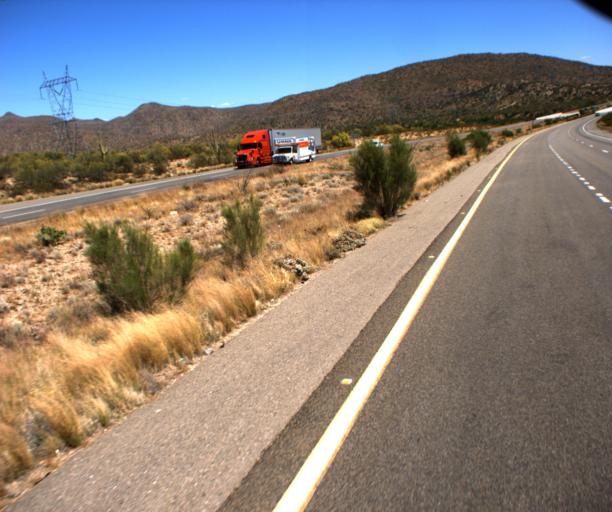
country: US
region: Arizona
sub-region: Yavapai County
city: Bagdad
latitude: 34.4267
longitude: -113.2445
